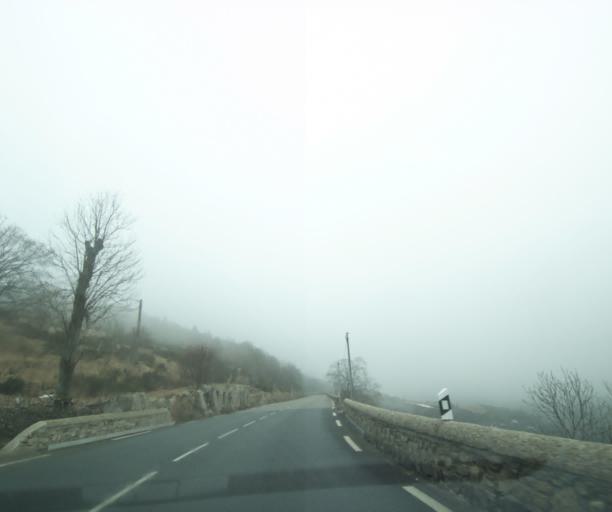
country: FR
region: Languedoc-Roussillon
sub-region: Departement de la Lozere
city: Langogne
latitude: 44.6961
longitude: 4.0269
